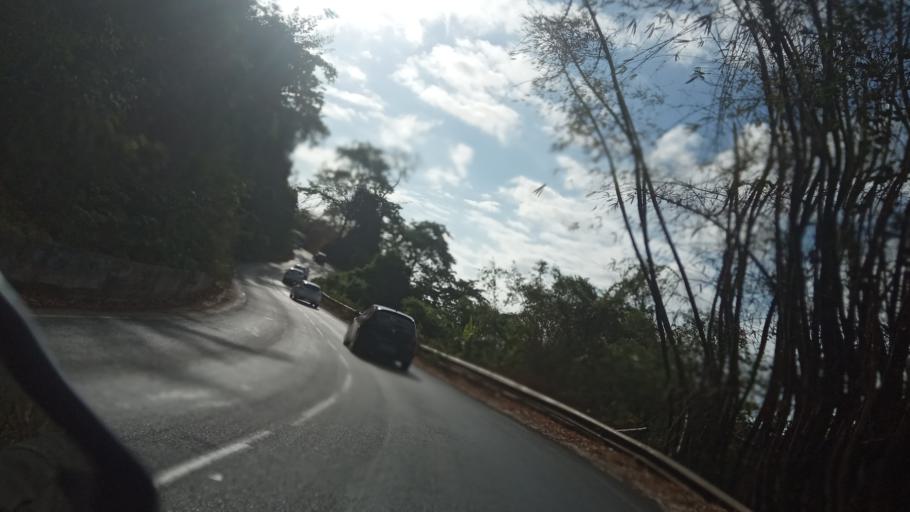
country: YT
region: Dembeni
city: Dembeni
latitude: -12.8377
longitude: 45.1828
